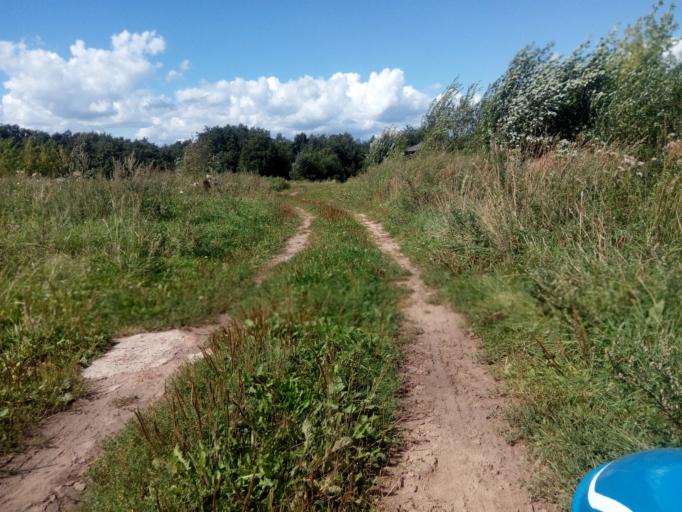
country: BY
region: Vitebsk
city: Dzisna
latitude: 55.6759
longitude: 28.3204
